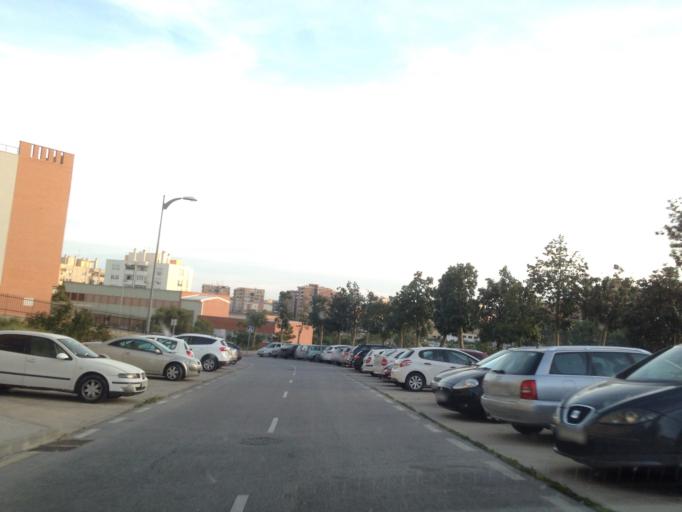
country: ES
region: Andalusia
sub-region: Provincia de Malaga
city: Malaga
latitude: 36.7275
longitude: -4.4459
